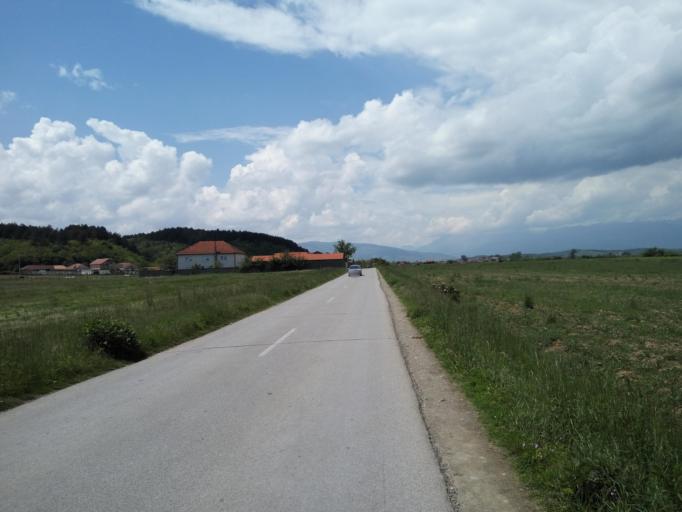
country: XK
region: Gjakova
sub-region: Komuna e Gjakoves
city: Gjakove
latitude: 42.3621
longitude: 20.4343
